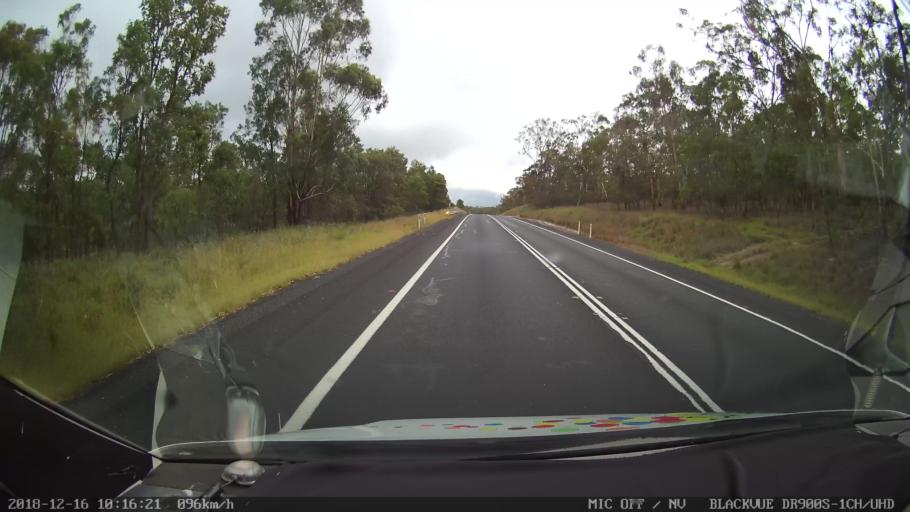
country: AU
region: New South Wales
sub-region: Tenterfield Municipality
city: Carrolls Creek
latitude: -29.2677
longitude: 151.9818
